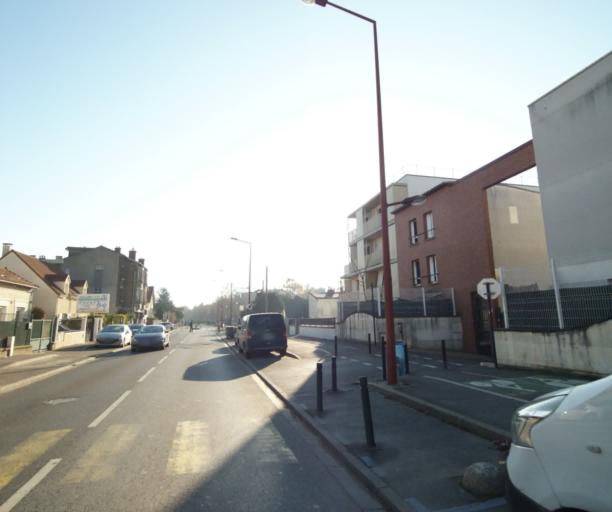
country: FR
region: Ile-de-France
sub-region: Departement du Val-d'Oise
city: Arnouville
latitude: 48.9950
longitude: 2.4225
